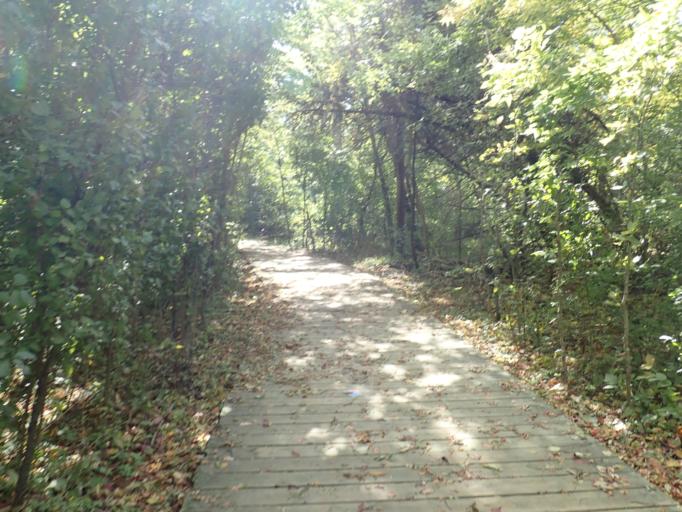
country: US
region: Ohio
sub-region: Erie County
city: Sandusky
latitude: 41.9134
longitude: -82.5094
